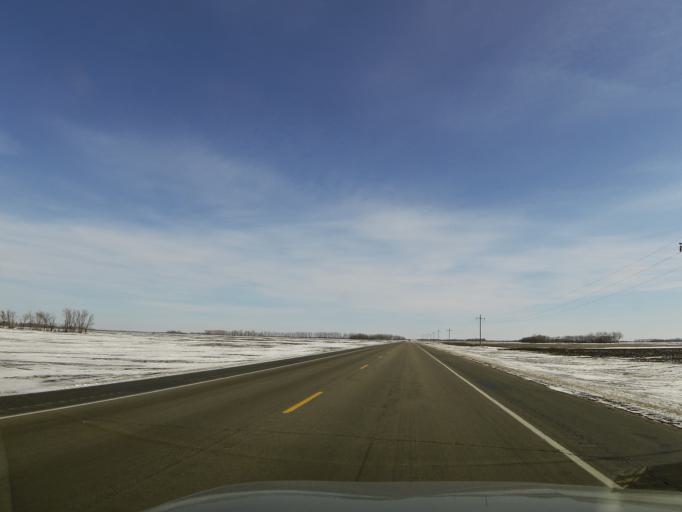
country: US
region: North Dakota
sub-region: Walsh County
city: Grafton
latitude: 48.4120
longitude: -97.2479
